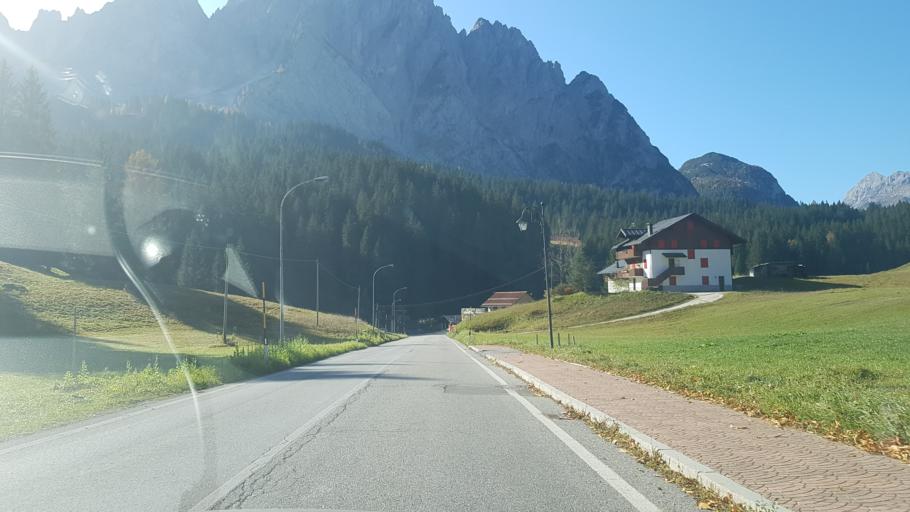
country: IT
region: Veneto
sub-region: Provincia di Belluno
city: Granvilla
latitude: 46.5678
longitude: 12.7204
